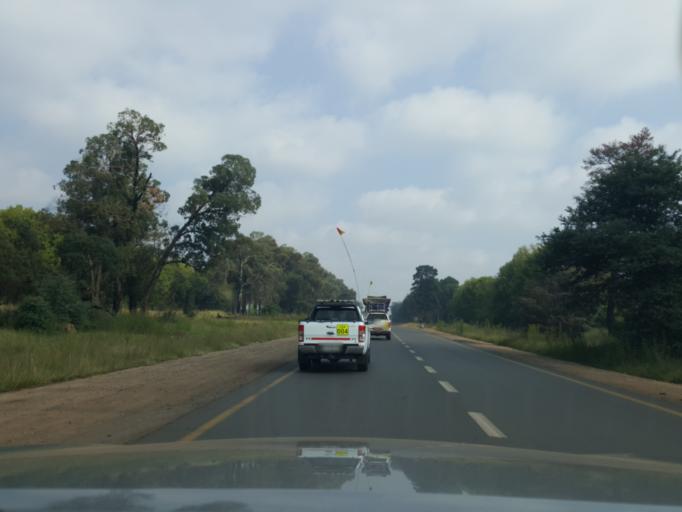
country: ZA
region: Mpumalanga
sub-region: Nkangala District Municipality
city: Witbank
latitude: -25.9875
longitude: 29.2876
